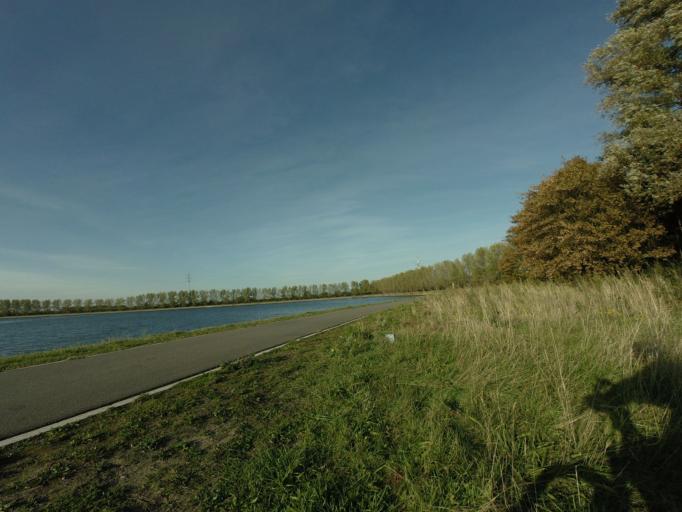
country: NL
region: North Brabant
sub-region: Gemeente Woensdrecht
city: Woensdrecht
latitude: 51.3699
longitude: 4.3020
